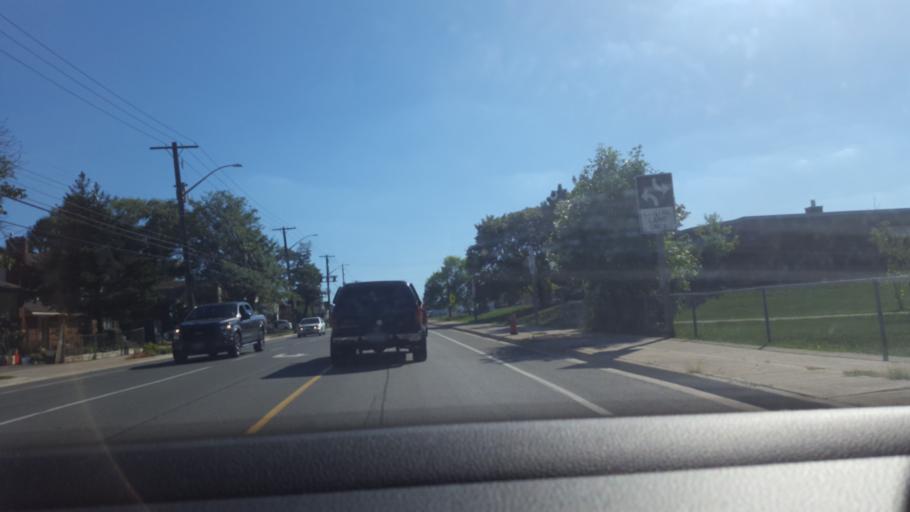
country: CA
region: Ontario
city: Hamilton
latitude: 43.2499
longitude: -79.7759
